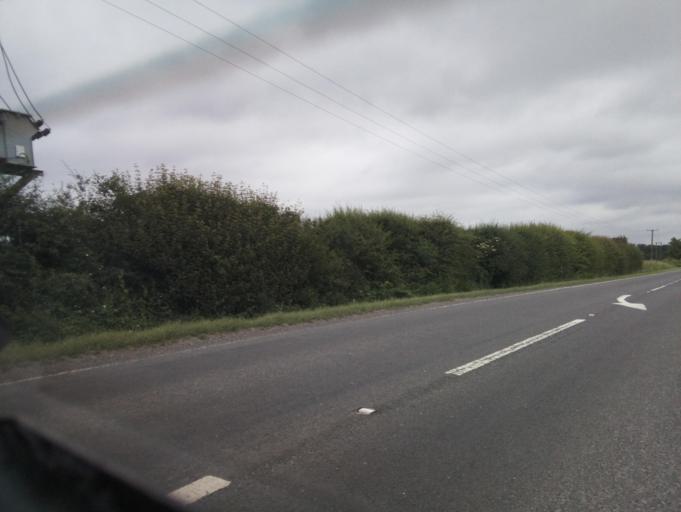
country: GB
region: England
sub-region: Nottinghamshire
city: East Leake
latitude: 52.8165
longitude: -1.1973
